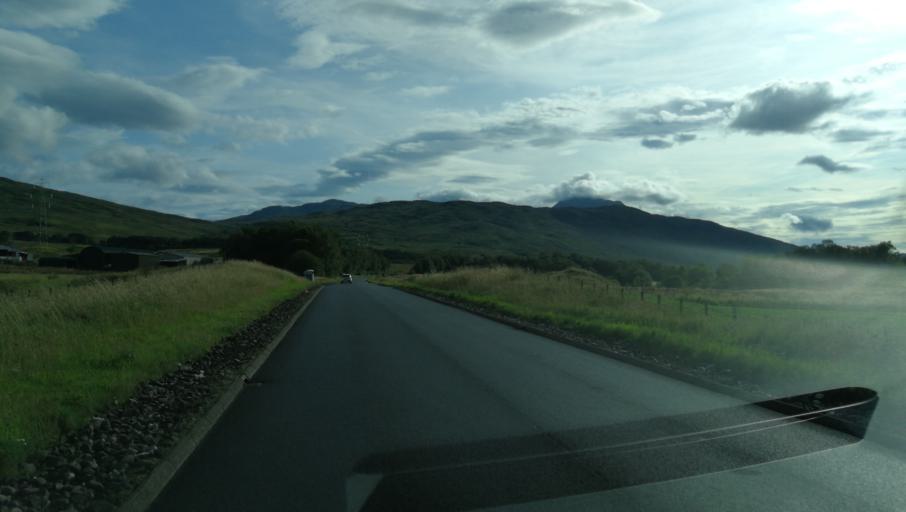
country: GB
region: Scotland
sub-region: Stirling
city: Callander
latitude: 56.4237
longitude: -4.4219
